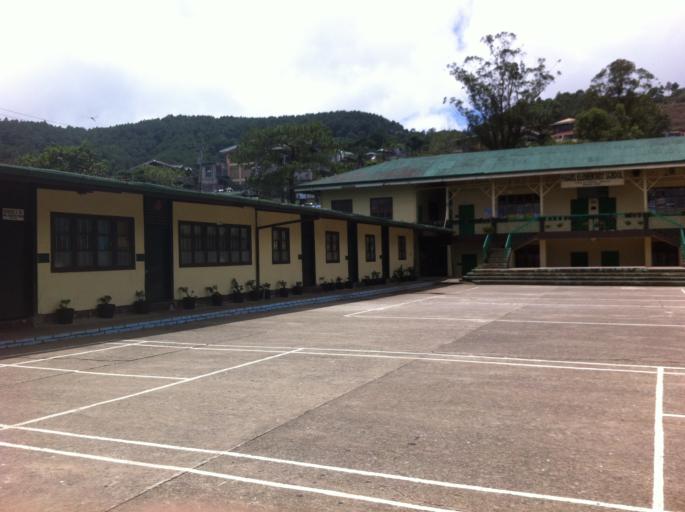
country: PH
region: Cordillera
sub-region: Province of Benguet
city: La Trinidad
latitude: 16.4481
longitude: 120.5762
